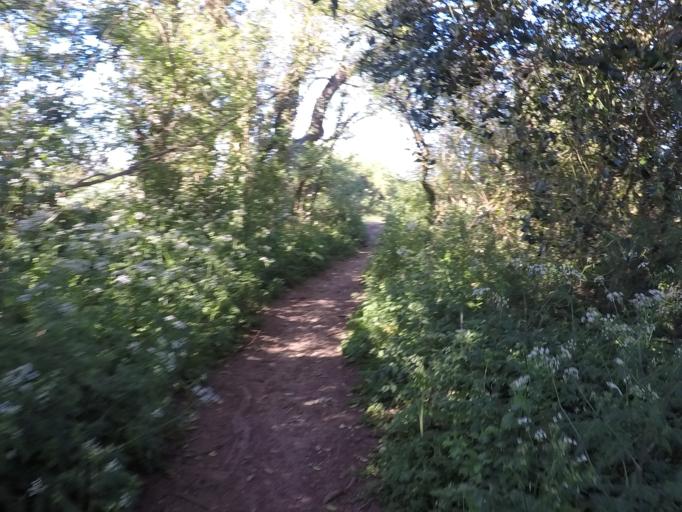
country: GB
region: England
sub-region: Oxfordshire
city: Stonesfield
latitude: 51.8597
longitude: -1.4377
